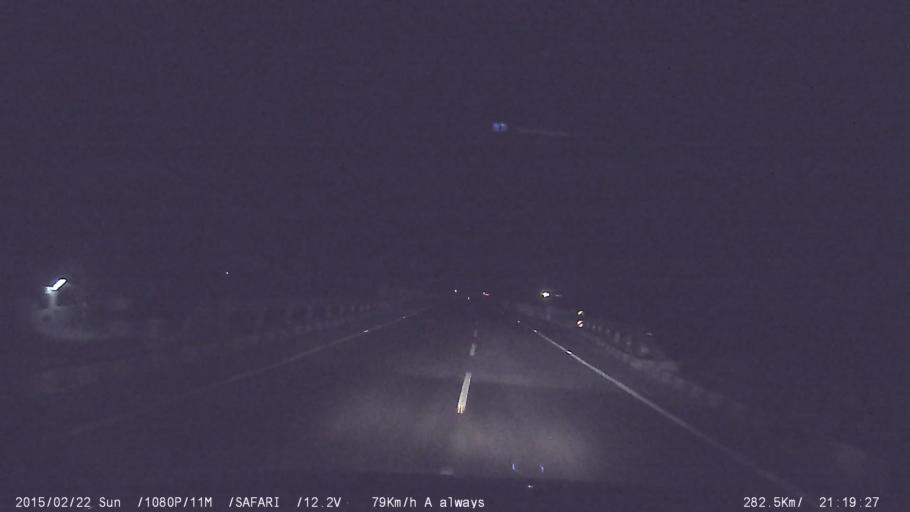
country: IN
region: Tamil Nadu
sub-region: Karur
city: Karur
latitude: 10.8479
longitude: 77.9732
